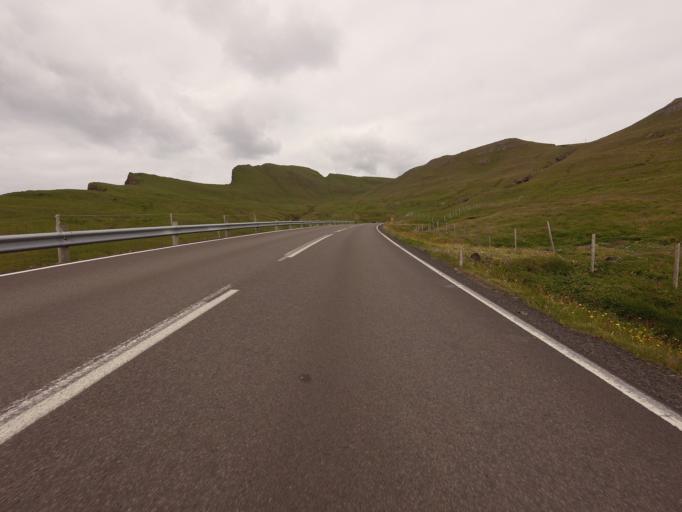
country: FO
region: Suduroy
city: Vagur
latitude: 61.4108
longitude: -6.7421
